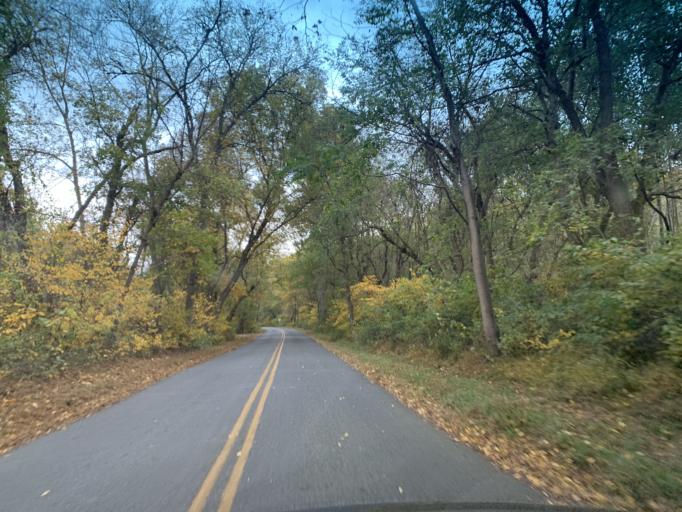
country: US
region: Maryland
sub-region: Harford County
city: Havre de Grace
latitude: 39.6177
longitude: -76.1543
